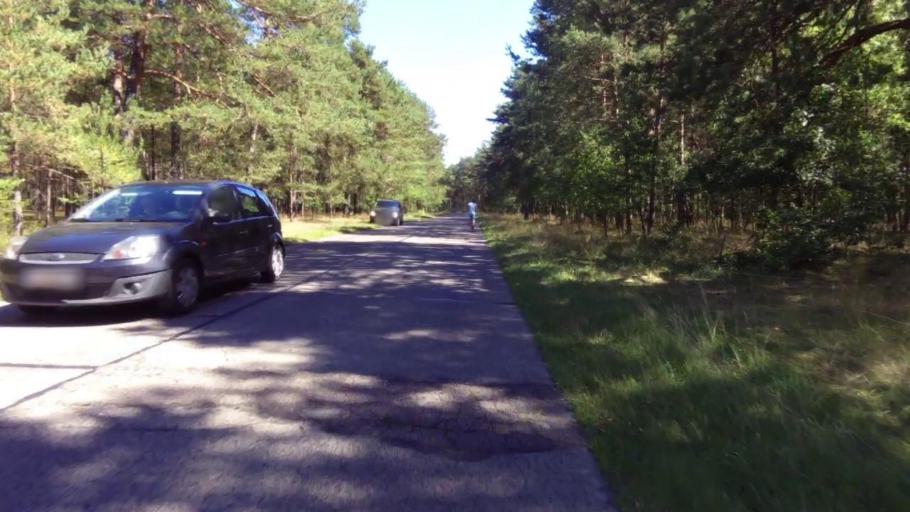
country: PL
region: West Pomeranian Voivodeship
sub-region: Powiat szczecinecki
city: Borne Sulinowo
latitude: 53.5856
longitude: 16.5046
